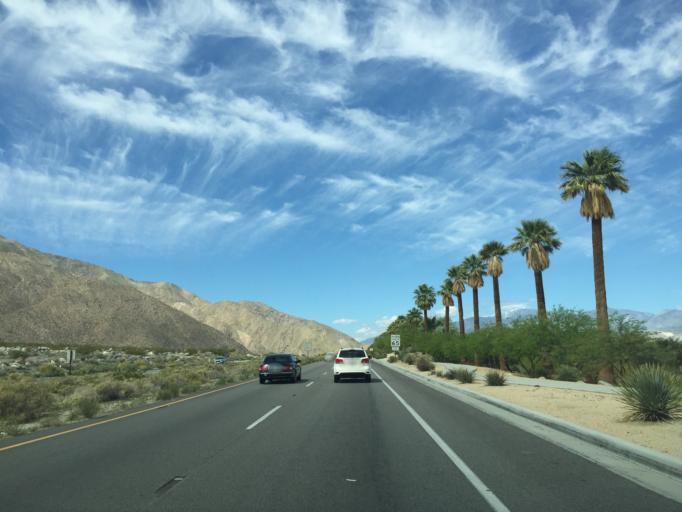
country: US
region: California
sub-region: Riverside County
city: Palm Springs
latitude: 33.8618
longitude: -116.5619
